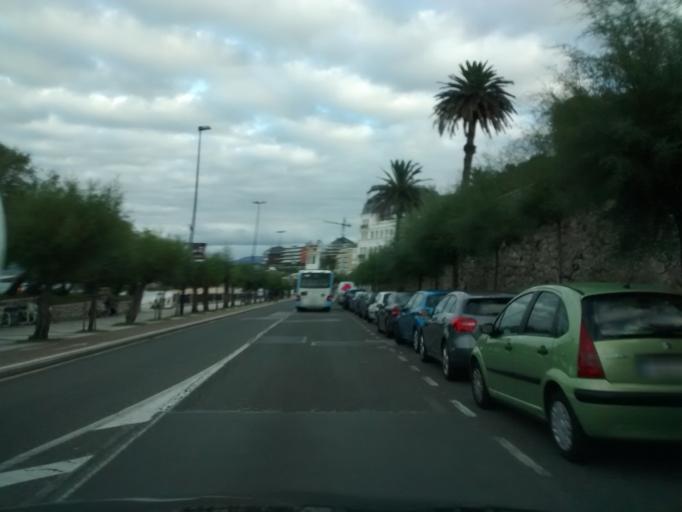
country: ES
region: Cantabria
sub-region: Provincia de Cantabria
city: Santander
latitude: 43.4736
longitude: -3.7845
